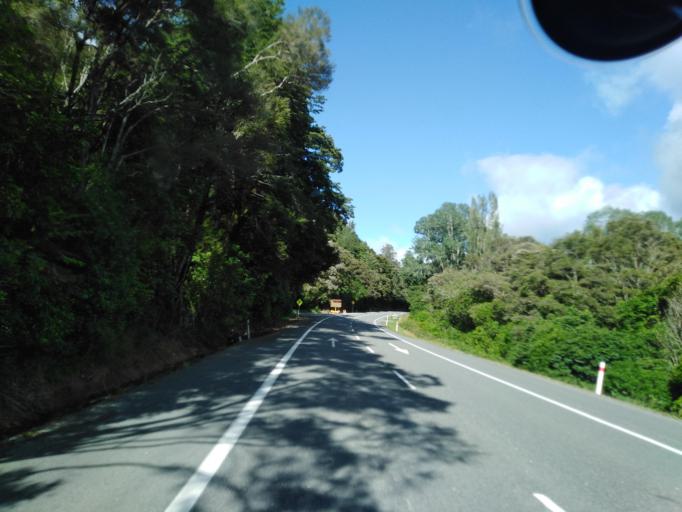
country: NZ
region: Nelson
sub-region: Nelson City
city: Nelson
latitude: -41.3011
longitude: 173.5787
